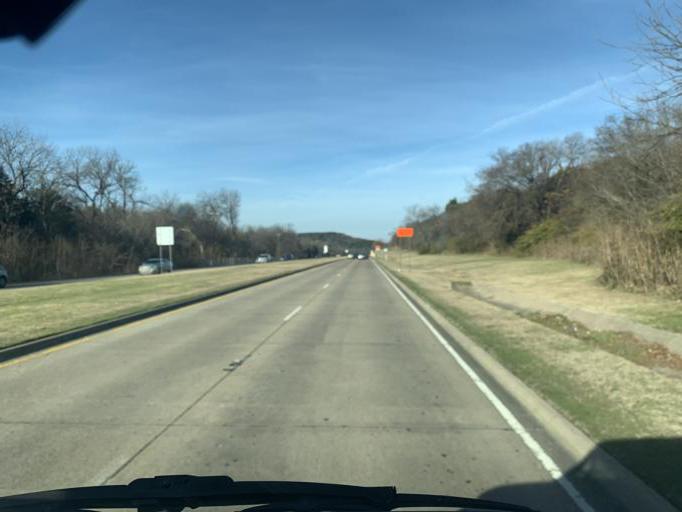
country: US
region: Texas
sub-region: Dallas County
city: Cedar Hill
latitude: 32.6115
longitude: -96.9604
